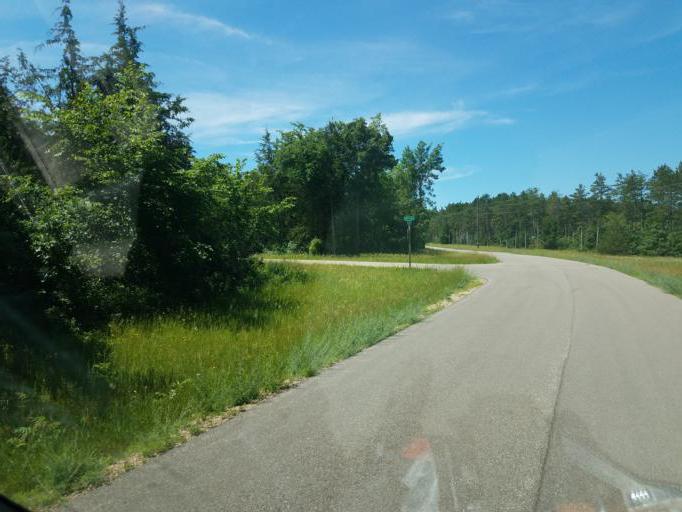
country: US
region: Wisconsin
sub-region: Juneau County
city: Mauston
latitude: 43.8692
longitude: -89.9473
